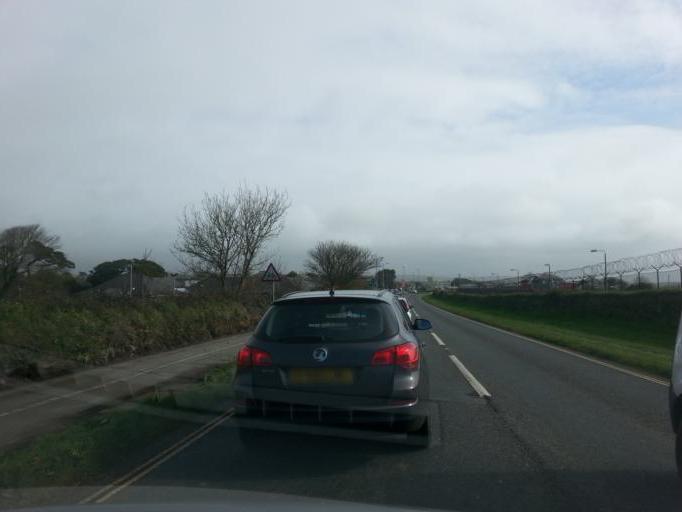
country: GB
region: England
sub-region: Cornwall
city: Helston
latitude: 50.0906
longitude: -5.2662
